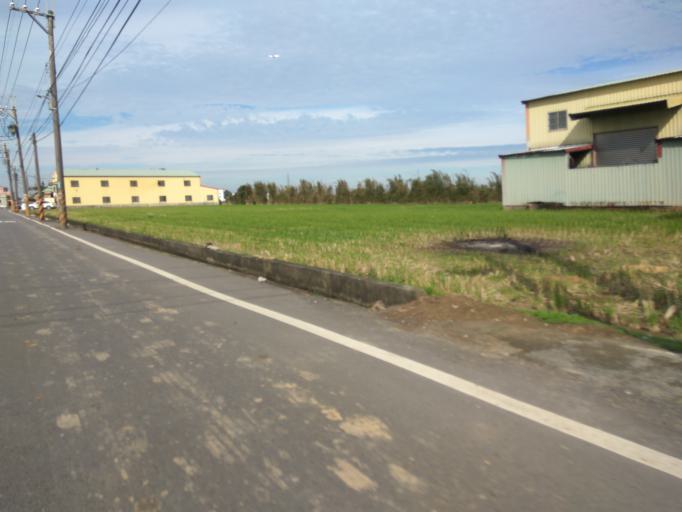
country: TW
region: Taiwan
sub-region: Hsinchu
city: Zhubei
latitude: 24.9520
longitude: 121.1311
